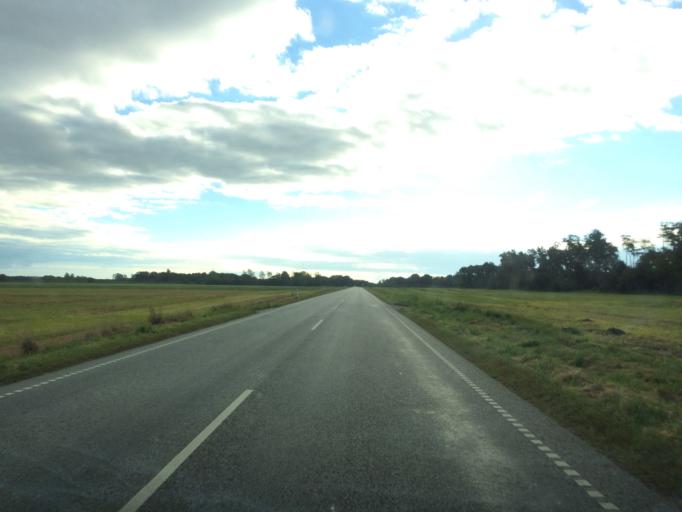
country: DK
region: Central Jutland
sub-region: Herning Kommune
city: Kibaek
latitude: 55.9469
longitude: 8.7581
